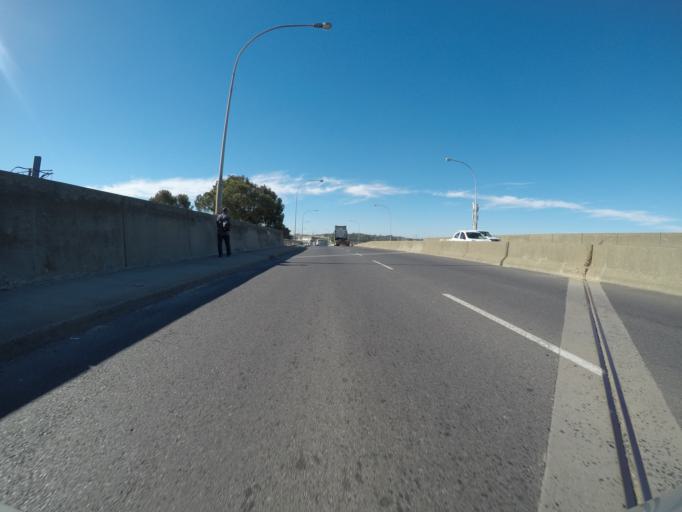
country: ZA
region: Western Cape
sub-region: City of Cape Town
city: Kraaifontein
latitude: -33.8931
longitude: 18.6725
